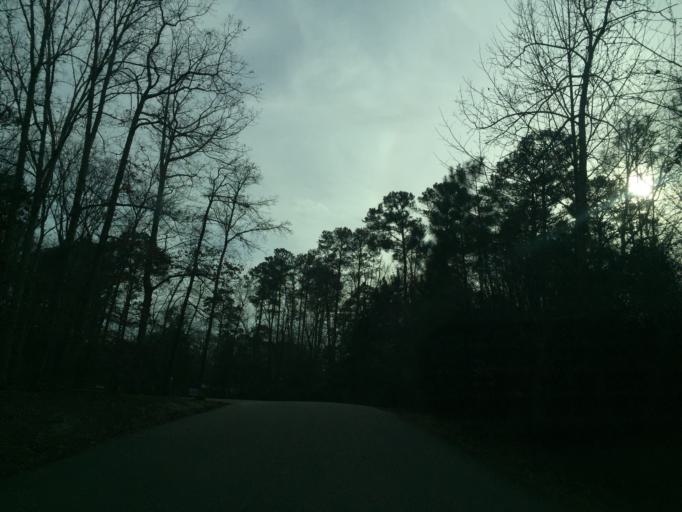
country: US
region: Virginia
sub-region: City of Newport News
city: Newport News
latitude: 37.0524
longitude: -76.4894
